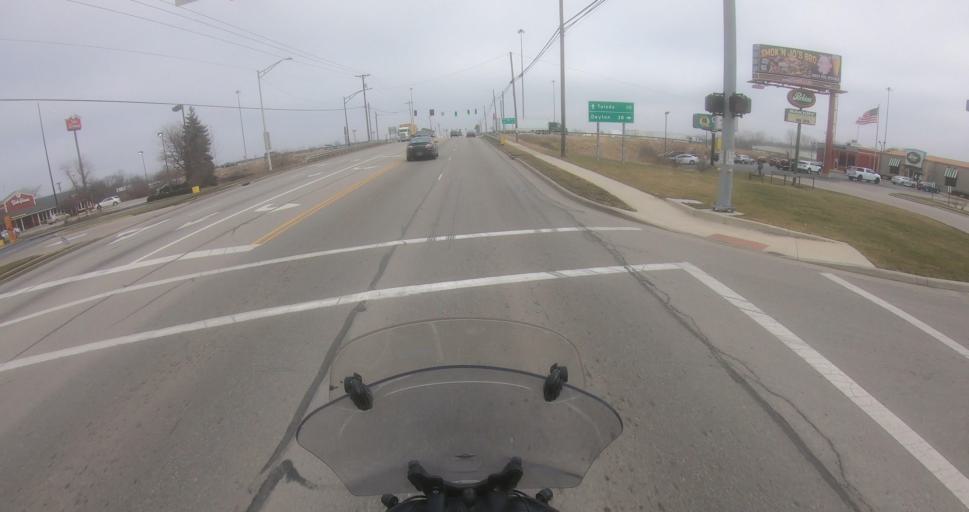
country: US
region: Ohio
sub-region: Shelby County
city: Sidney
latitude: 40.2878
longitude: -84.1846
